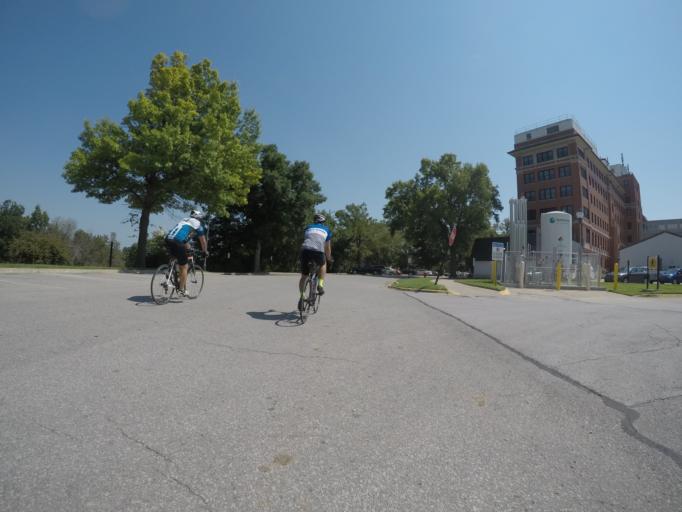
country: US
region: Kansas
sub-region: Leavenworth County
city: Lansing
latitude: 39.2832
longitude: -94.8960
